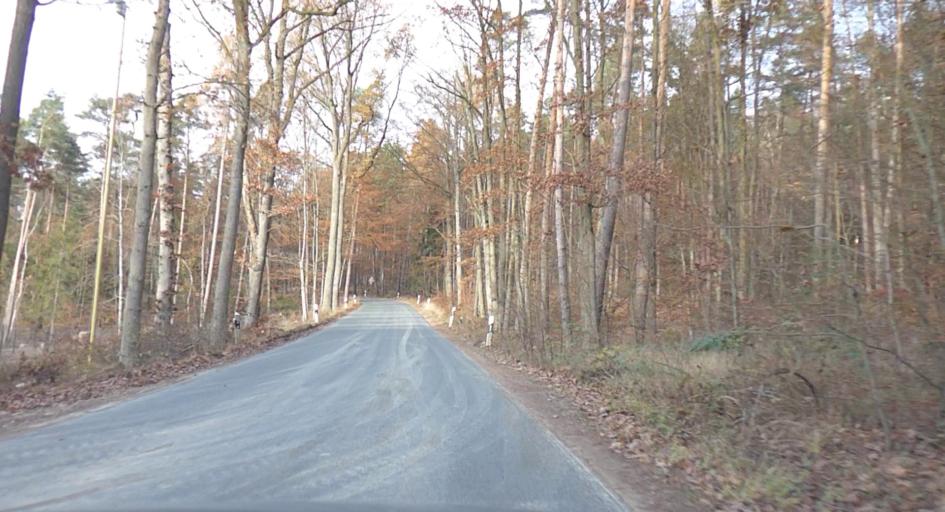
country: DE
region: Bavaria
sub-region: Regierungsbezirk Mittelfranken
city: Bubenreuth
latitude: 49.6131
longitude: 11.0241
